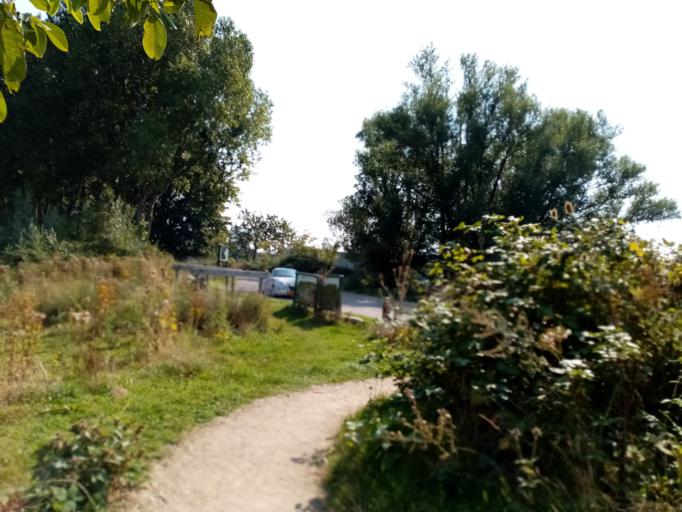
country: NL
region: South Holland
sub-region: Gemeente Rotterdam
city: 's-Gravenland
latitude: 51.8980
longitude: 4.5304
